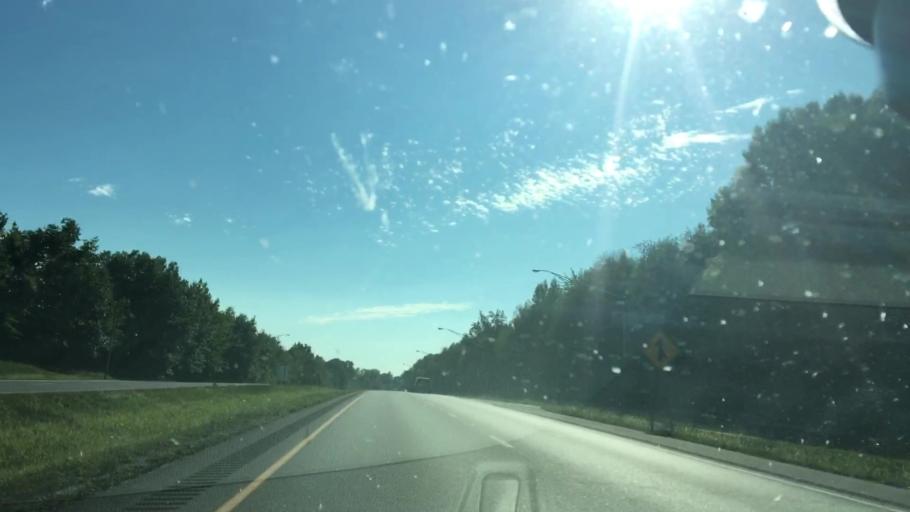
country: US
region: Kentucky
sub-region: Daviess County
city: Owensboro
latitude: 37.7306
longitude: -87.0905
